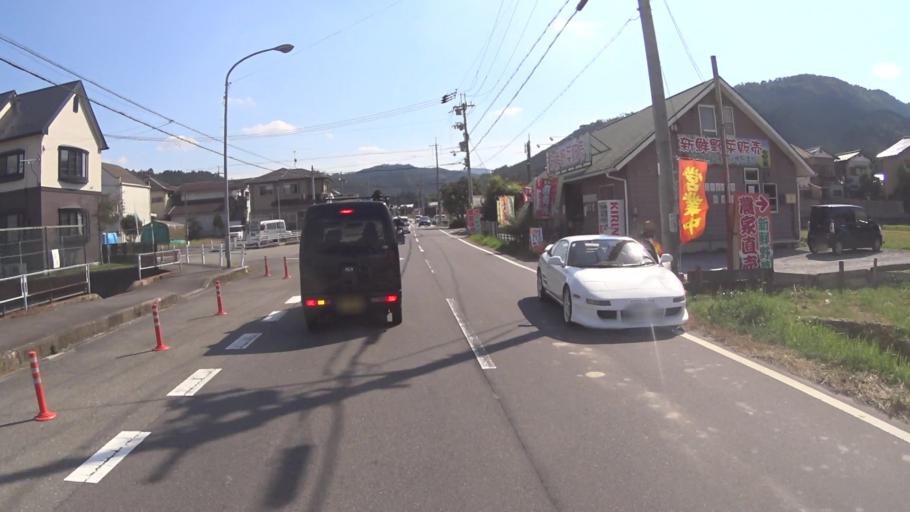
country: JP
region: Kyoto
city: Kameoka
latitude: 35.0011
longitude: 135.5781
